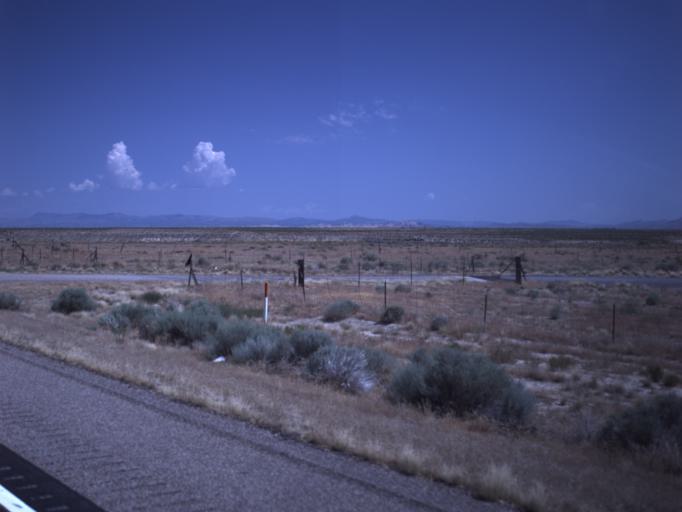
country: US
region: Utah
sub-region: Millard County
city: Delta
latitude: 39.3890
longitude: -112.4990
